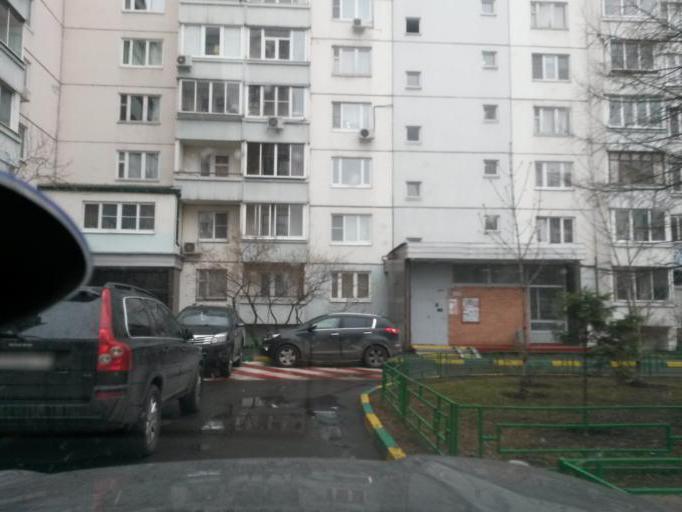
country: RU
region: Moscow
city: Brateyevo
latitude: 55.6531
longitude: 37.7726
